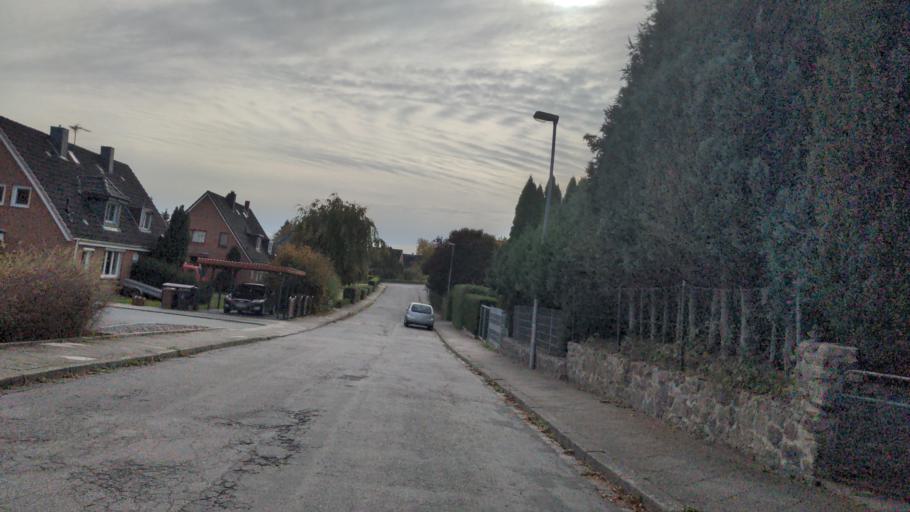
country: DE
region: Mecklenburg-Vorpommern
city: Selmsdorf
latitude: 53.9150
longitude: 10.8219
